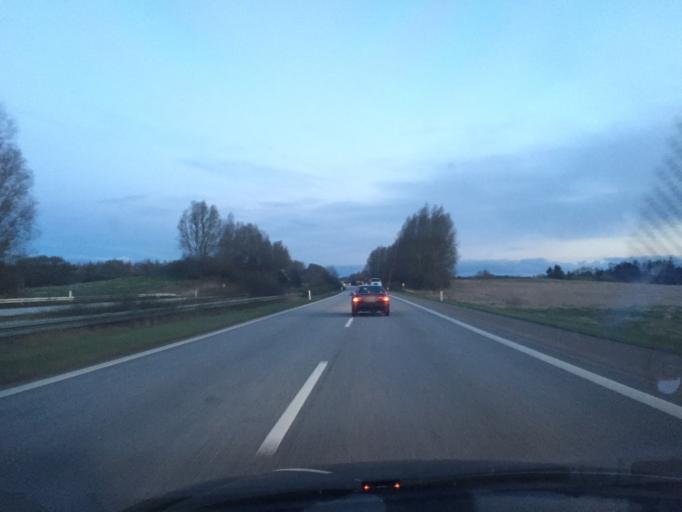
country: DK
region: Capital Region
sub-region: Fredensborg Kommune
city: Niva
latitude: 55.9471
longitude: 12.4781
